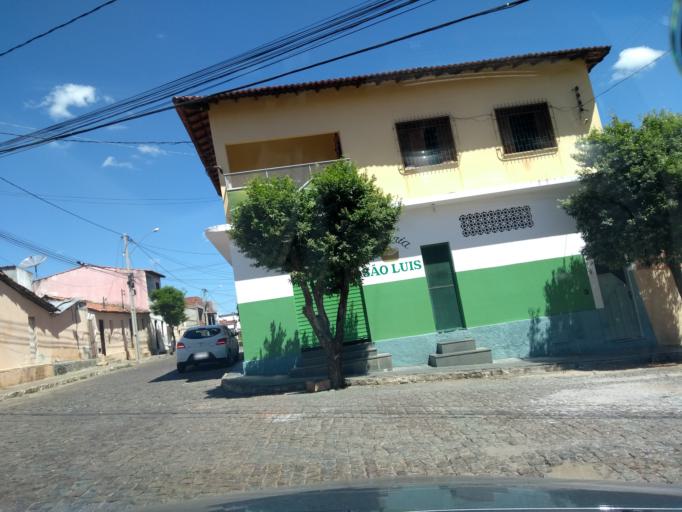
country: BR
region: Bahia
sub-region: Brumado
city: Brumado
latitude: -14.2069
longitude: -41.6710
